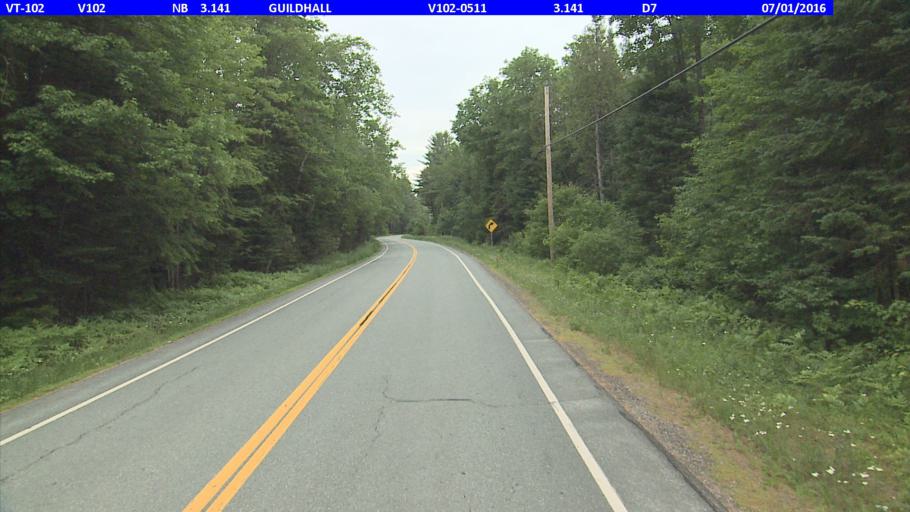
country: US
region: New Hampshire
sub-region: Coos County
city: Northumberland
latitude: 44.5382
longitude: -71.5841
